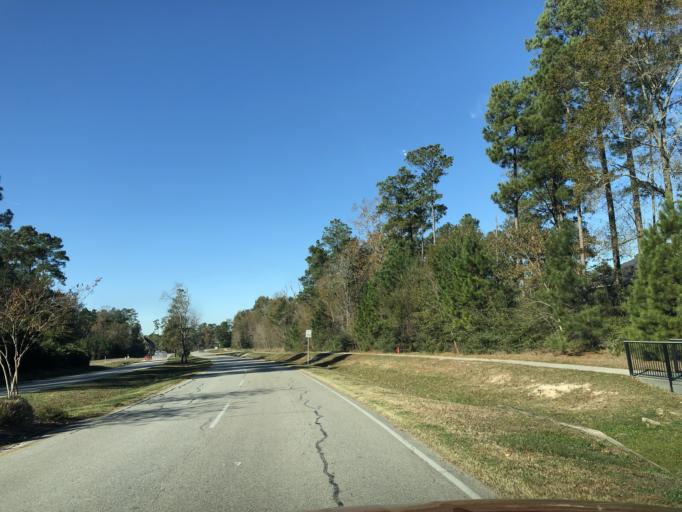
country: US
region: Texas
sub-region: Montgomery County
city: Porter Heights
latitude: 30.0874
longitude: -95.3382
